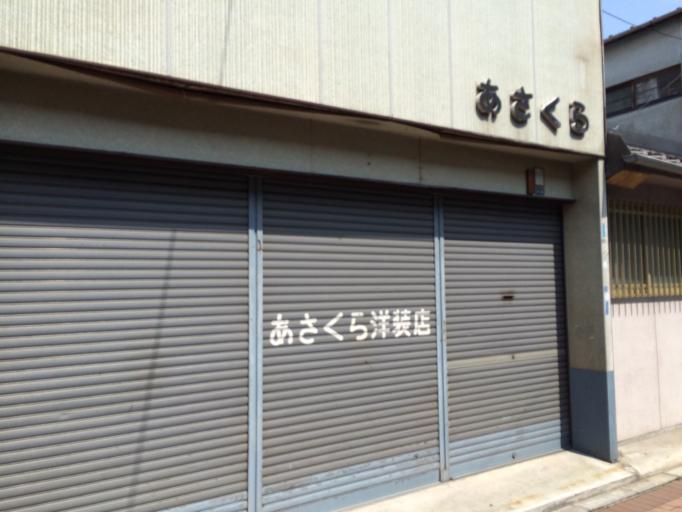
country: JP
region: Okayama
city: Kurashiki
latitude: 34.5996
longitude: 133.7668
